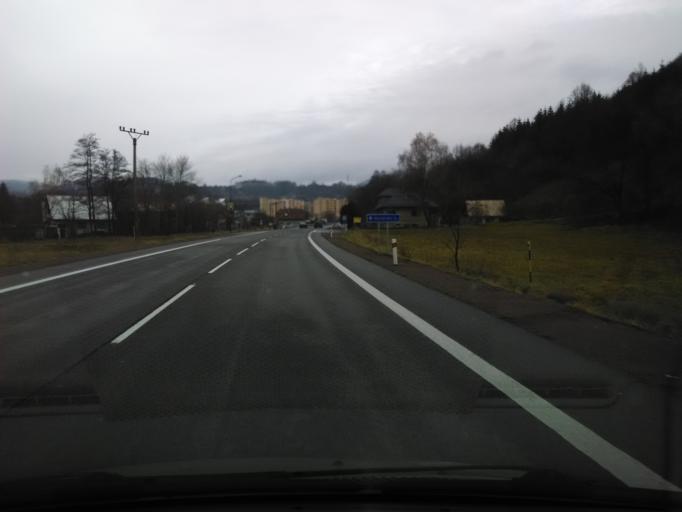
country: SK
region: Banskobystricky
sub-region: Okres Ziar nad Hronom
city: Kremnica
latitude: 48.6721
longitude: 18.9101
